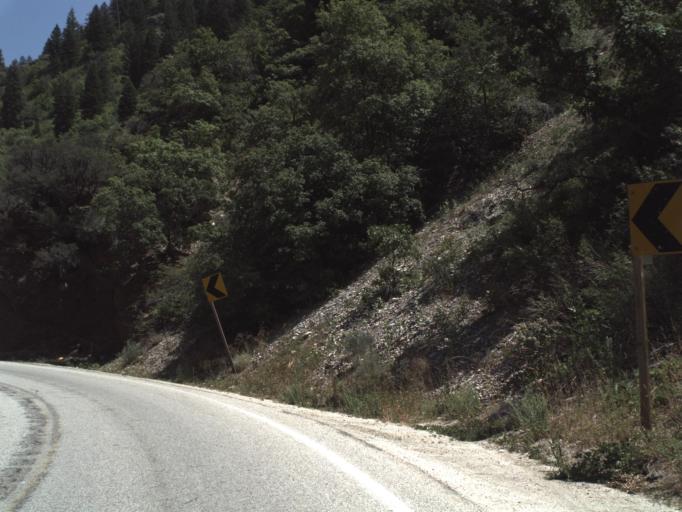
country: US
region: Utah
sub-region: Weber County
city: Ogden
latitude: 41.2379
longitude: -111.9124
